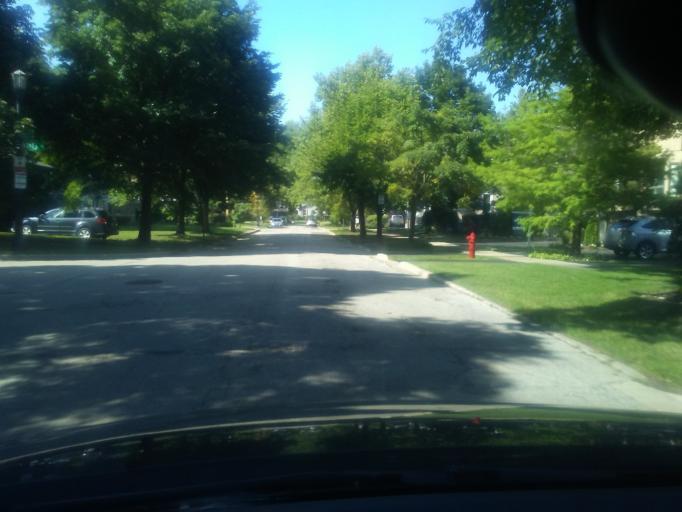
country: US
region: Illinois
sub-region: Cook County
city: Evanston
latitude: 42.0581
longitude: -87.6988
